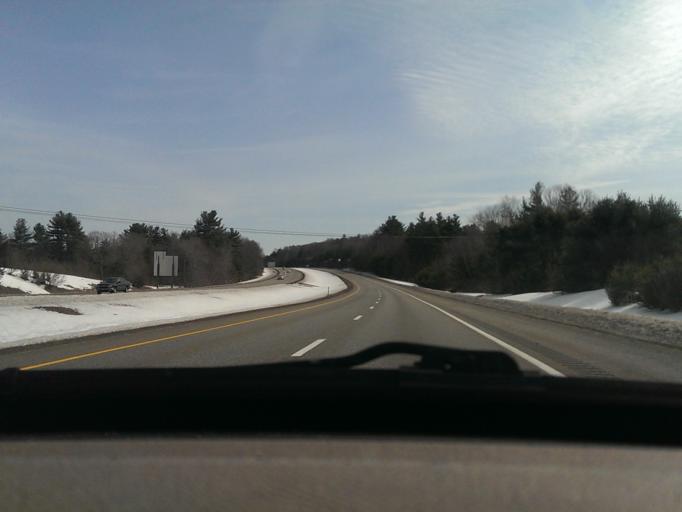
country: US
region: Massachusetts
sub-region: Worcester County
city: Millville
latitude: 42.0338
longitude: -71.6203
